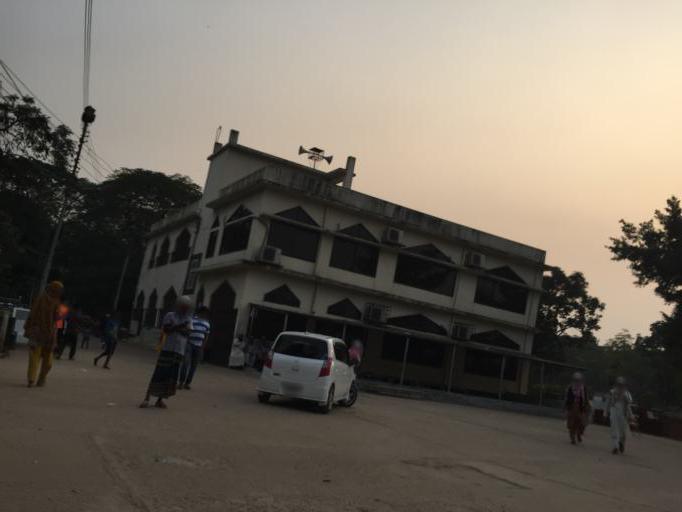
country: BD
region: Dhaka
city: Azimpur
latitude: 23.7953
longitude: 90.3463
